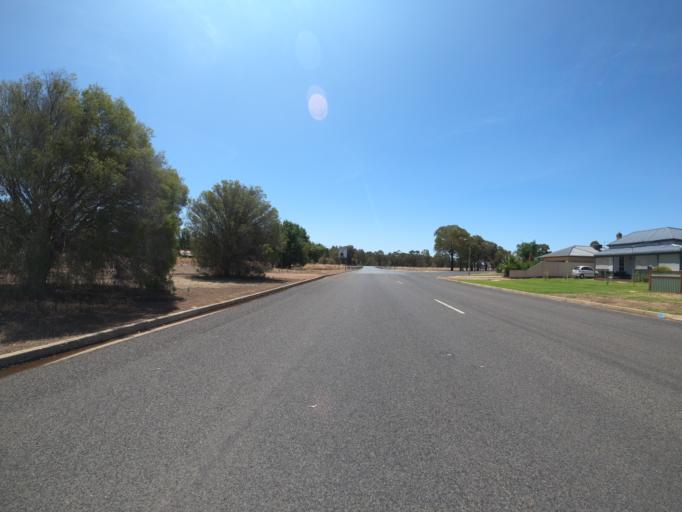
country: AU
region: Victoria
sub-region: Moira
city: Yarrawonga
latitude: -36.0183
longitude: 145.9955
